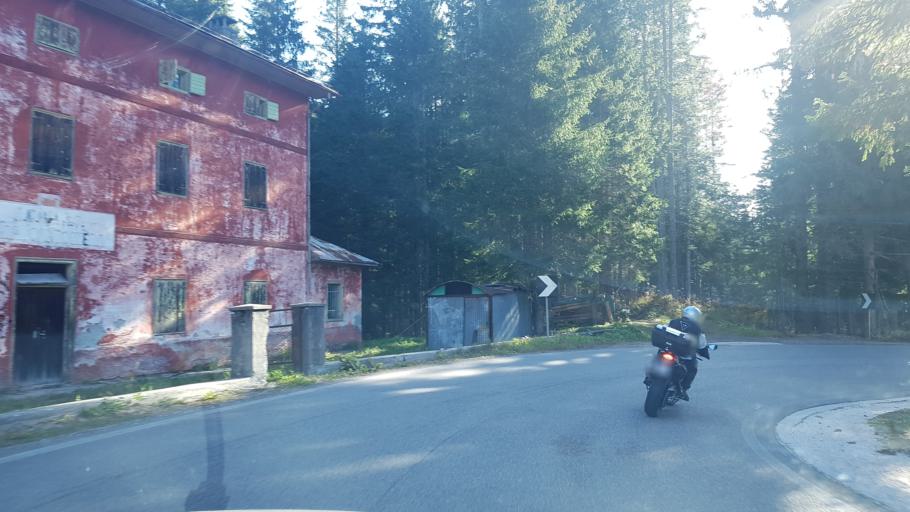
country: IT
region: Veneto
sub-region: Provincia di Belluno
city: Candide
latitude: 46.6460
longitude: 12.4517
